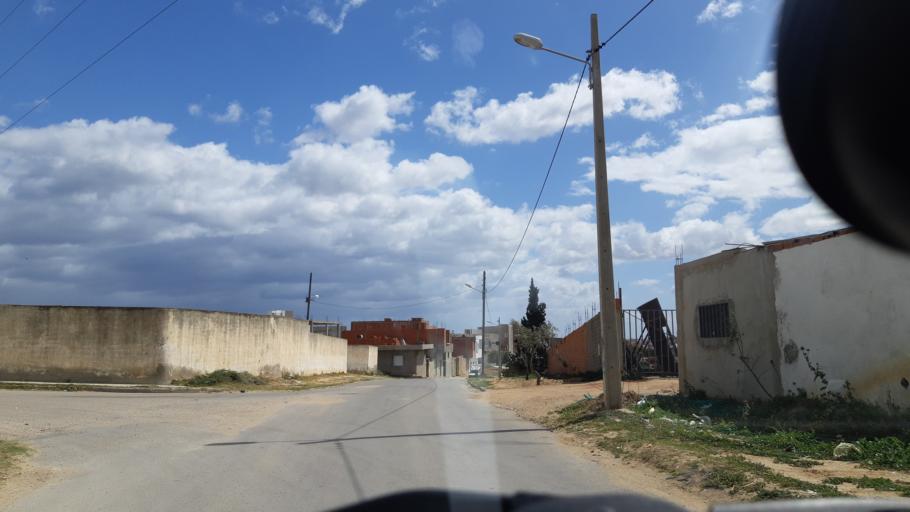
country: TN
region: Susah
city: Akouda
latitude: 35.8783
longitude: 10.5145
